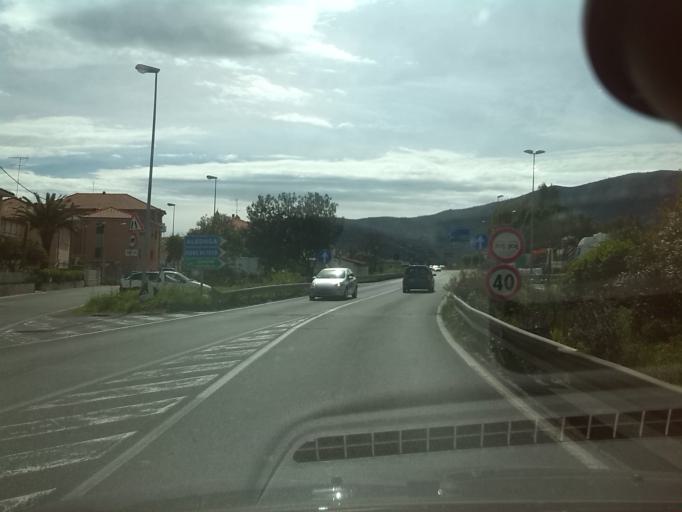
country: IT
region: Liguria
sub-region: Provincia di Savona
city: San Fedele-Lusignano
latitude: 44.0636
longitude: 8.1788
